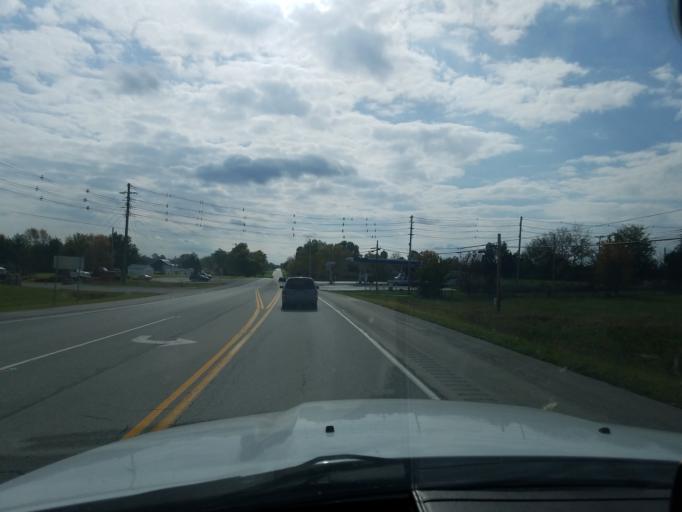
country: US
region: Kentucky
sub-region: Nelson County
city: Bardstown
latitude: 37.8986
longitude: -85.4734
